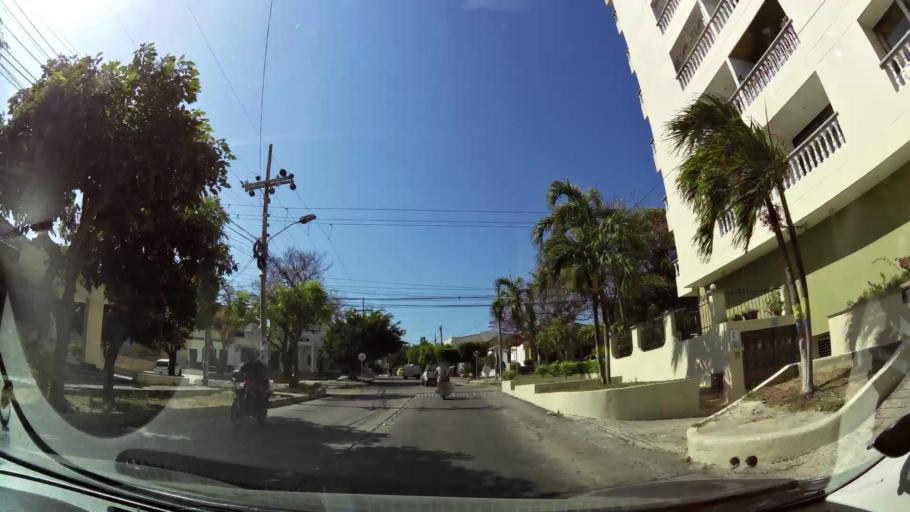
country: CO
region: Atlantico
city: Barranquilla
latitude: 10.9868
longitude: -74.8031
